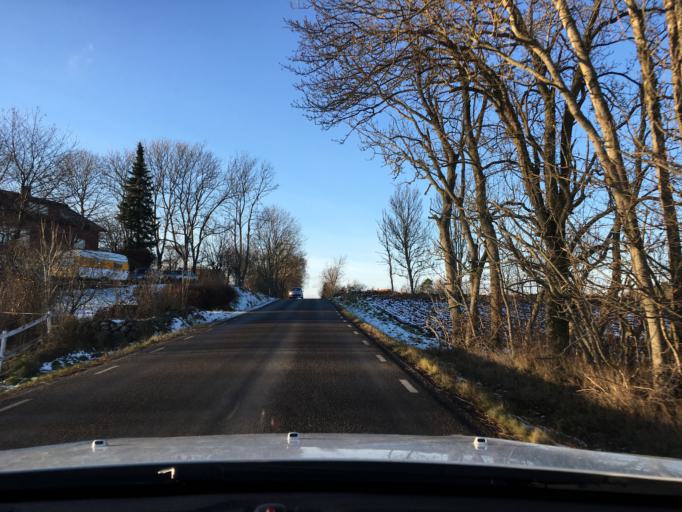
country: SE
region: Vaestra Goetaland
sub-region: Tjorns Kommun
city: Myggenas
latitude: 58.0496
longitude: 11.7151
